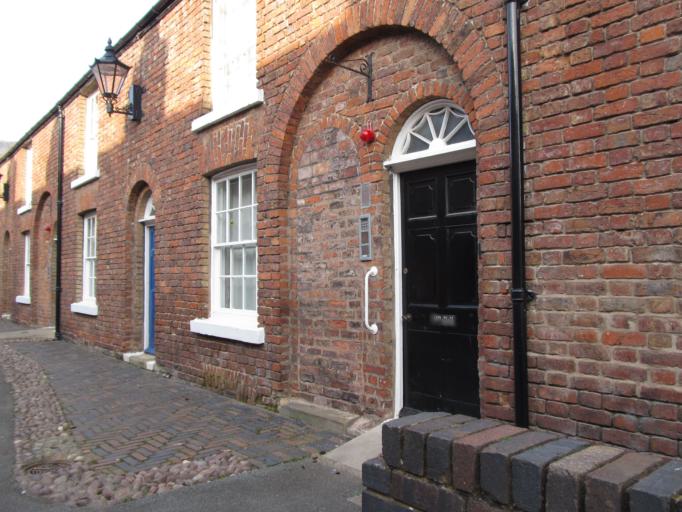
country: GB
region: Wales
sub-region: County of Flintshire
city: Holywell
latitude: 53.2730
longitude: -3.2216
